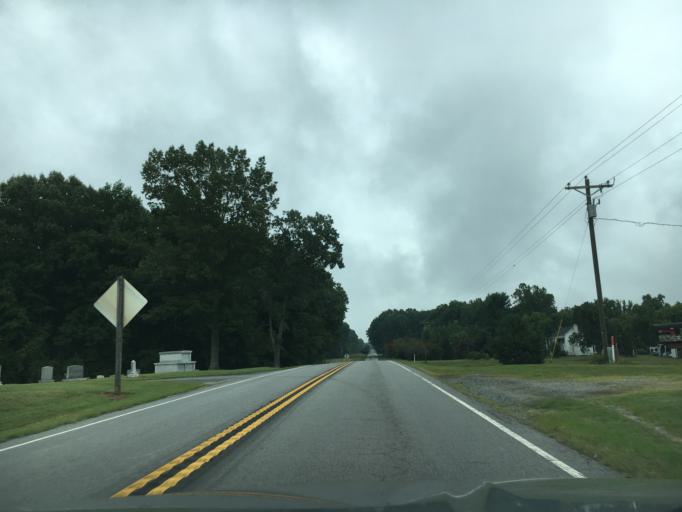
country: US
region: Virginia
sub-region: Halifax County
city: Mountain Road
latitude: 36.8692
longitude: -79.0119
